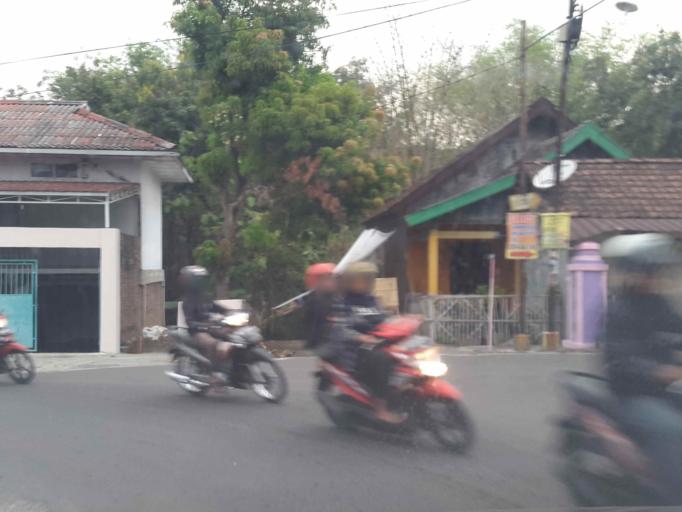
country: ID
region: Central Java
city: Jaten
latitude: -7.5573
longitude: 110.8693
